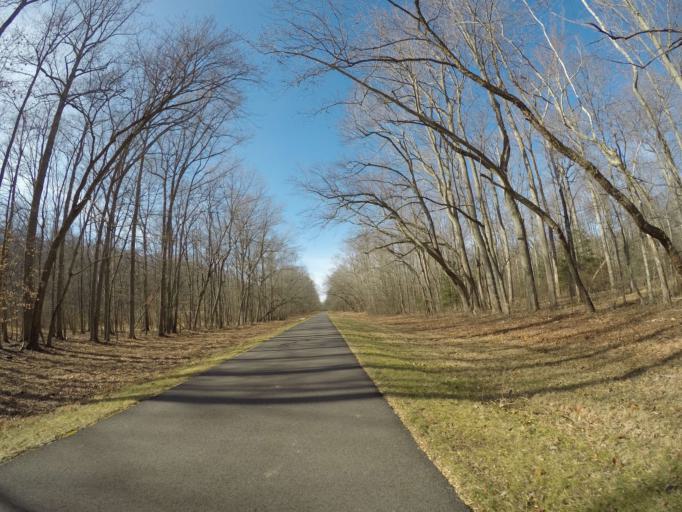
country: US
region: Maryland
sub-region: Charles County
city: Bennsville
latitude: 38.5958
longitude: -77.0276
